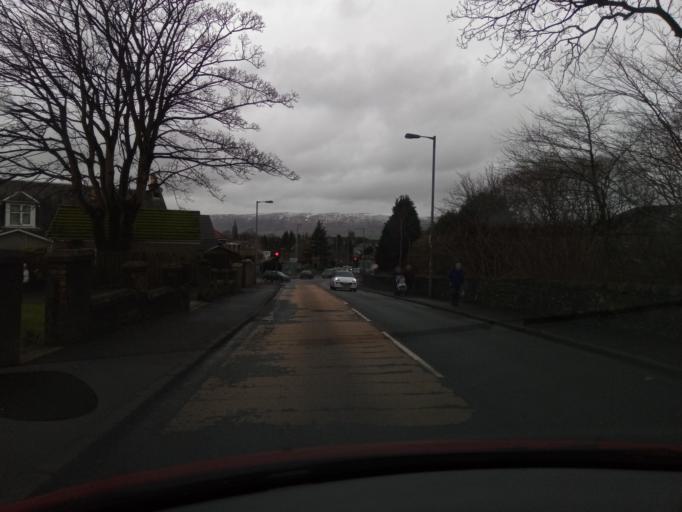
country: GB
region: Scotland
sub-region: East Dunbartonshire
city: Kirkintilloch
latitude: 55.9305
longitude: -4.1534
